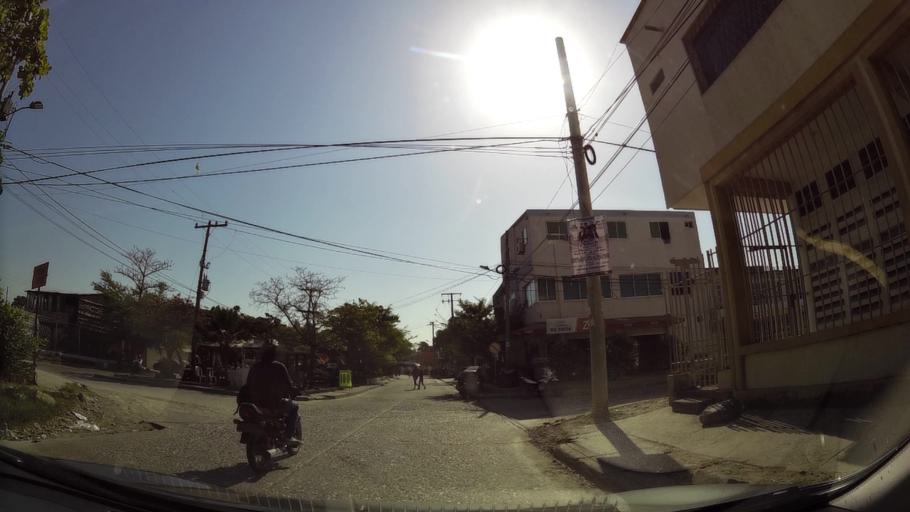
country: CO
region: Bolivar
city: Cartagena
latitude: 10.3724
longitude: -75.5034
